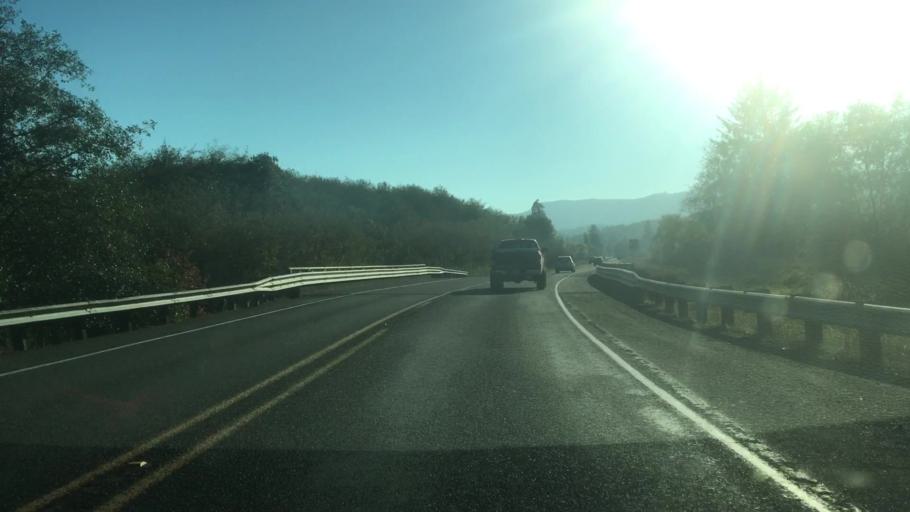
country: US
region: Oregon
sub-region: Clatsop County
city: Astoria
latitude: 46.3739
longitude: -123.8033
